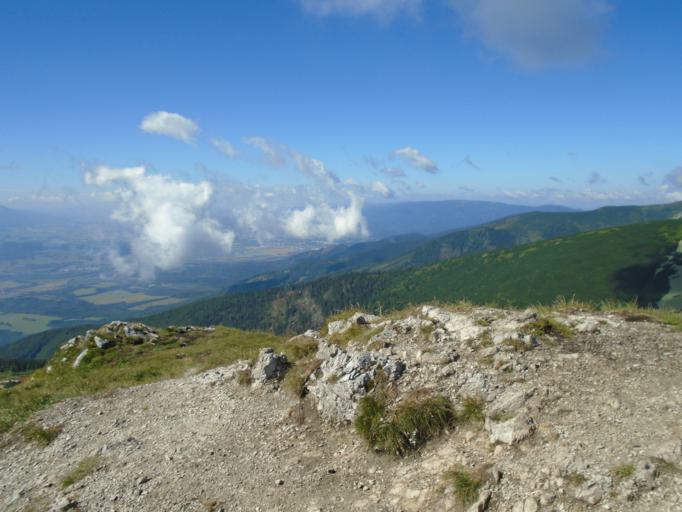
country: SK
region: Zilinsky
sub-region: Okres Zilina
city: Terchova
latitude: 49.1881
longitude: 19.0330
